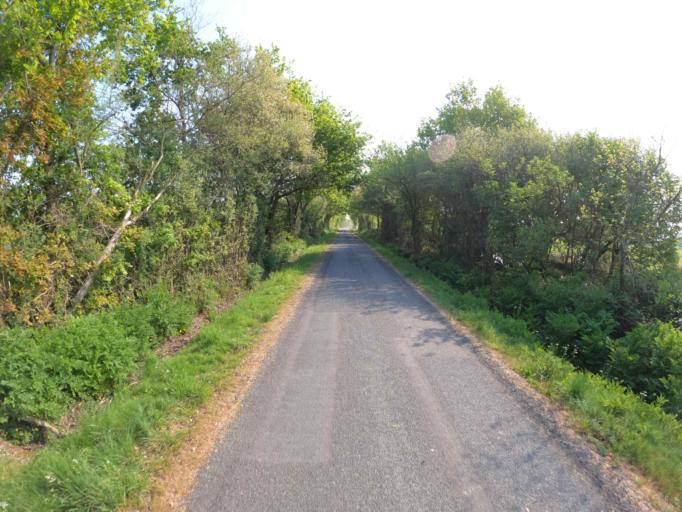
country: FR
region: Pays de la Loire
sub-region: Departement de la Vendee
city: Treize-Septiers
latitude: 47.0044
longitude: -1.2232
